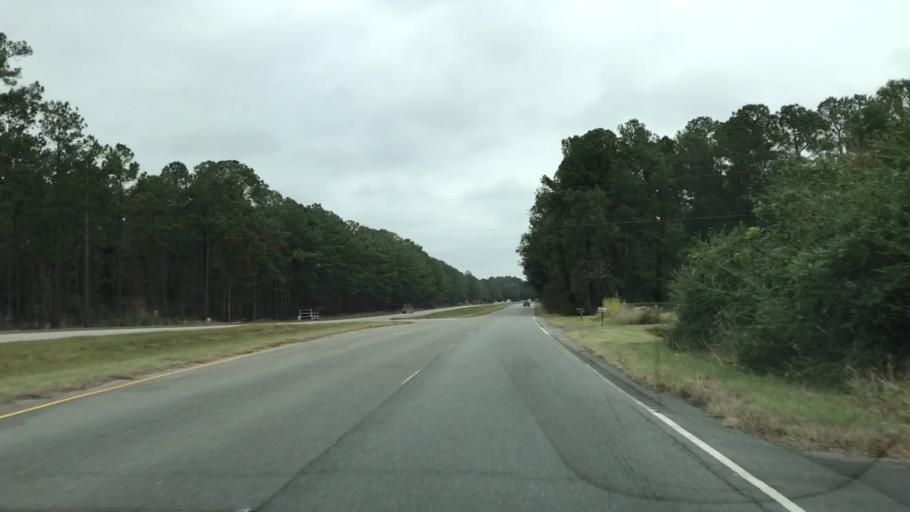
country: US
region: South Carolina
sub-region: Charleston County
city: Awendaw
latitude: 33.0319
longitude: -79.6235
